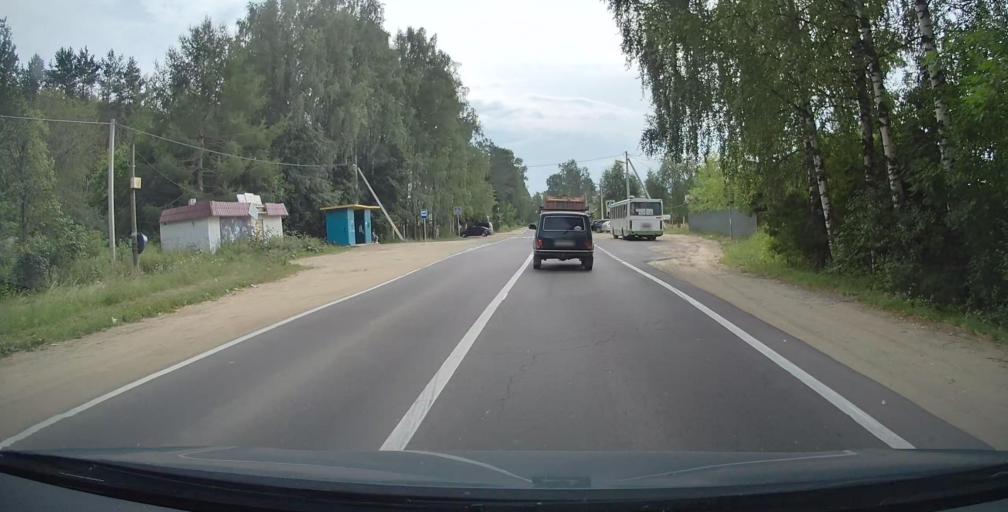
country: RU
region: Jaroslavl
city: Rybinsk
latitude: 57.9998
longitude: 38.7572
